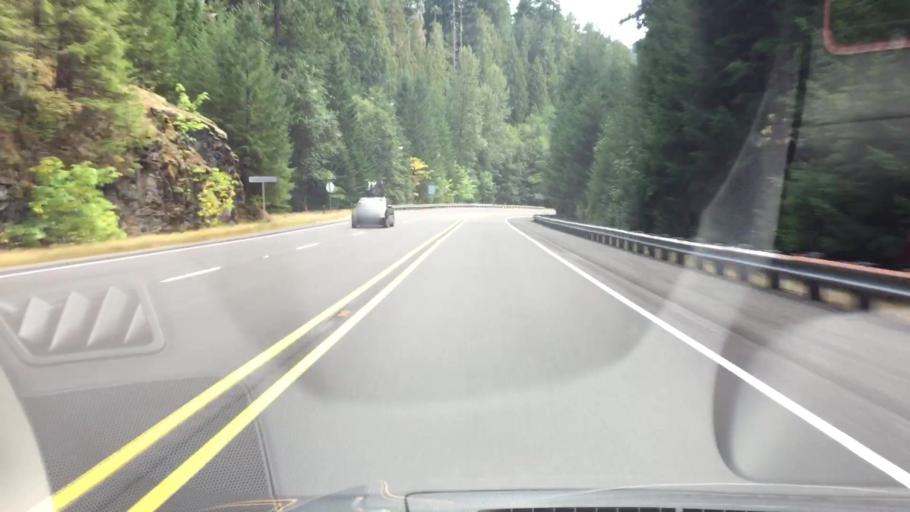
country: US
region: Washington
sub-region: Pierce County
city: Buckley
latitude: 46.6564
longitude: -121.6022
